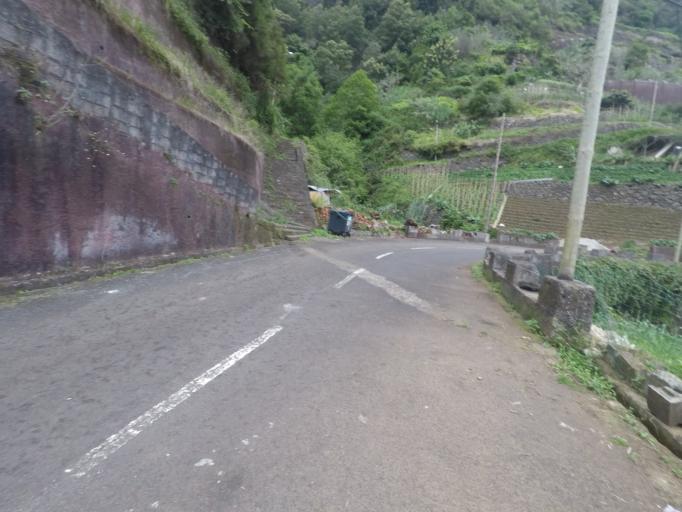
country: PT
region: Madeira
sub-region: Santana
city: Santana
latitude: 32.7665
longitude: -16.8760
